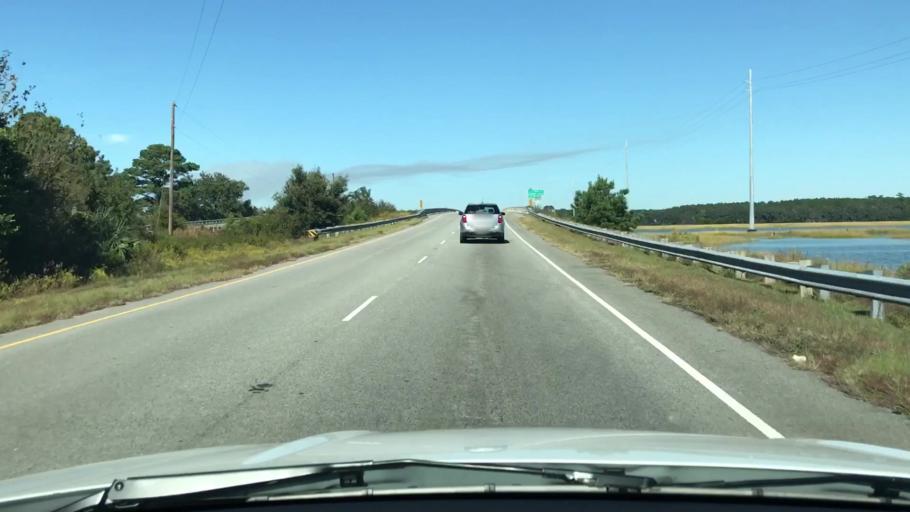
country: US
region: South Carolina
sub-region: Beaufort County
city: Laurel Bay
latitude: 32.5375
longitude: -80.7458
